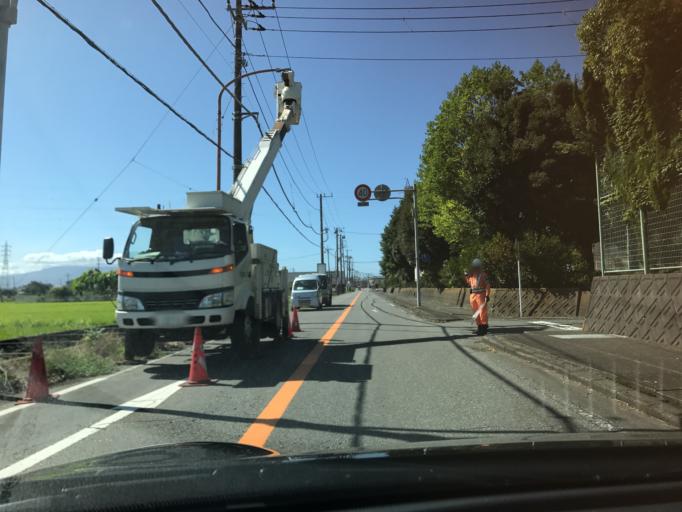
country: JP
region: Shizuoka
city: Numazu
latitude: 35.1277
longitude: 138.8110
